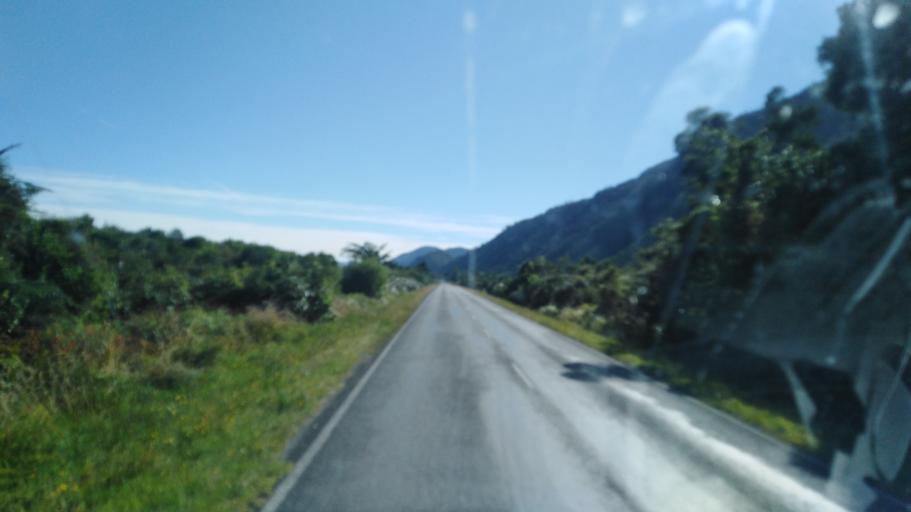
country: NZ
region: West Coast
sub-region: Buller District
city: Westport
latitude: -41.6488
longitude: 171.8336
